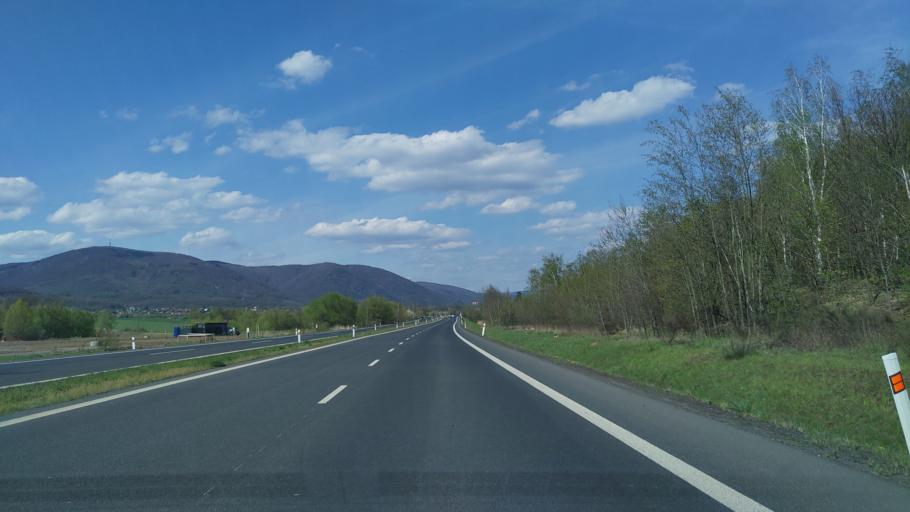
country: CZ
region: Ustecky
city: Jirkov
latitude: 50.4997
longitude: 13.4652
